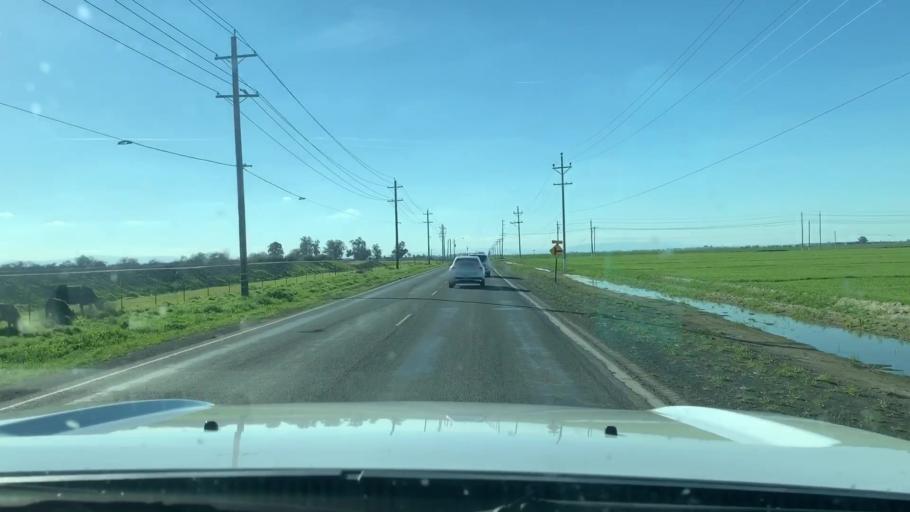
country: US
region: California
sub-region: Kings County
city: Home Garden
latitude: 36.2112
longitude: -119.6517
